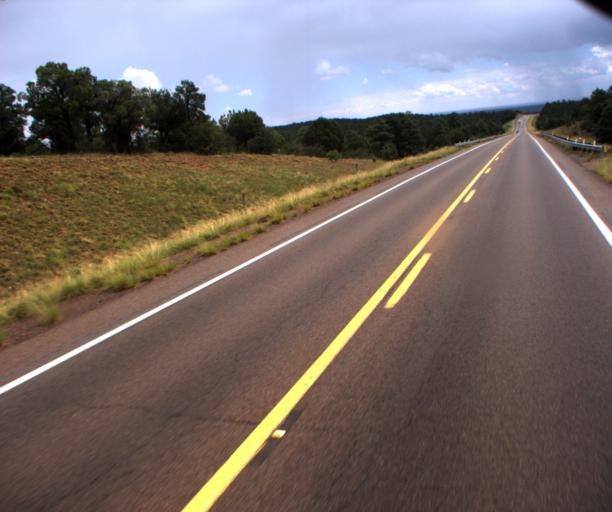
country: US
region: Arizona
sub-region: Navajo County
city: Heber-Overgaard
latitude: 34.3674
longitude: -110.3769
